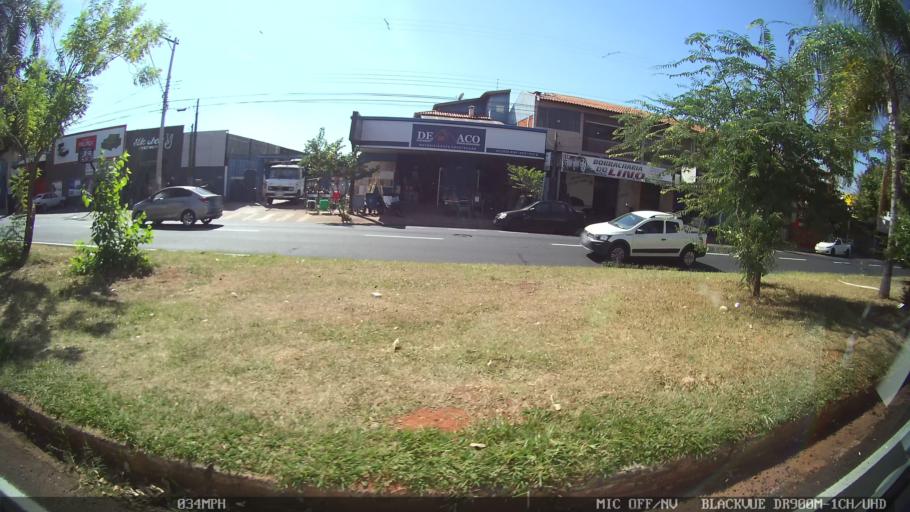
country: BR
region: Sao Paulo
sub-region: Sao Jose Do Rio Preto
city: Sao Jose do Rio Preto
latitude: -20.7766
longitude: -49.4079
